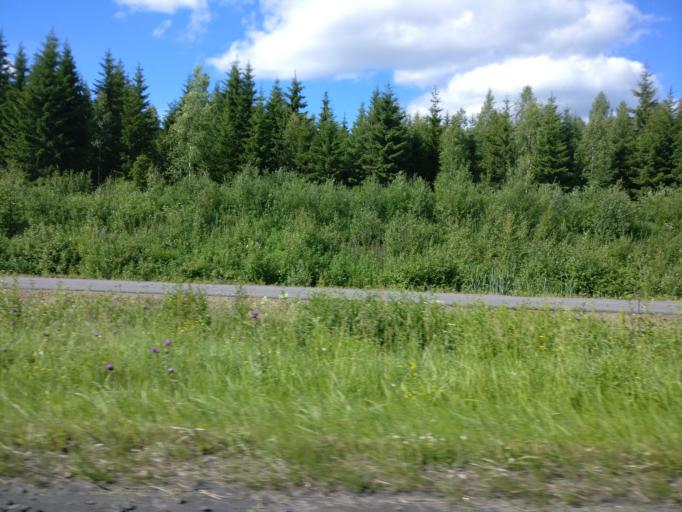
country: FI
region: Southern Savonia
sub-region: Savonlinna
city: Savonlinna
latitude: 61.8800
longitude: 29.0247
